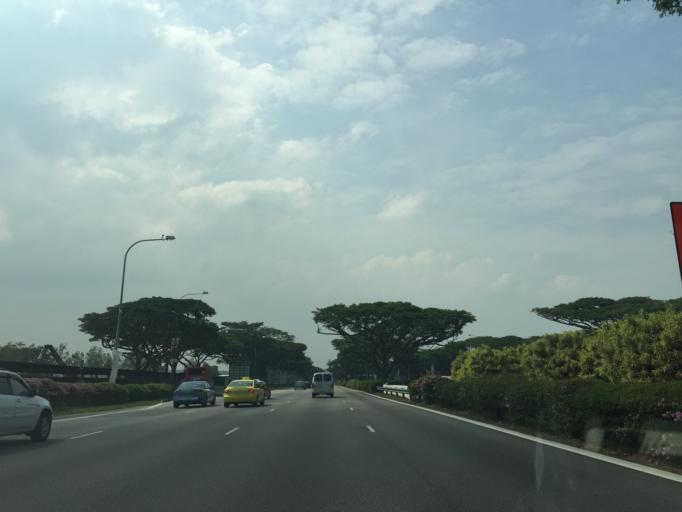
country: SG
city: Singapore
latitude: 1.3412
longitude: 103.9816
